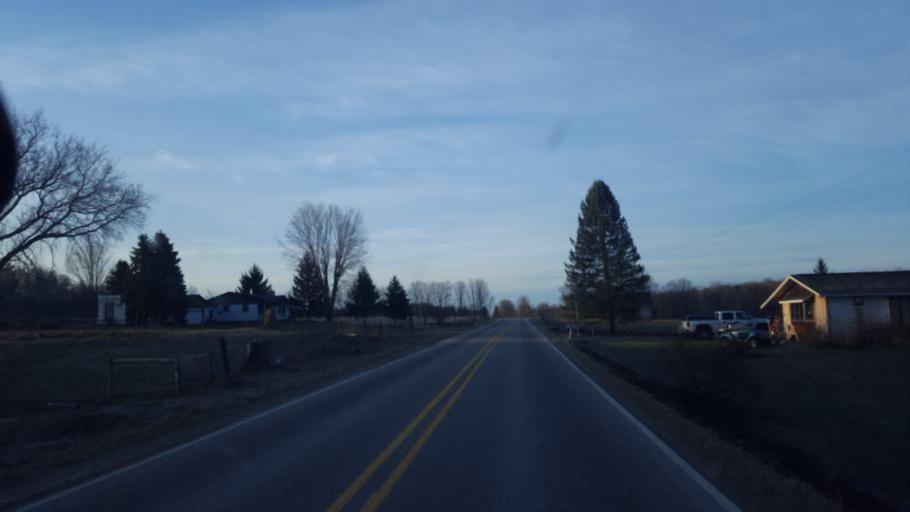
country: US
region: Michigan
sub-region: Isabella County
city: Lake Isabella
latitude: 43.5337
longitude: -85.0261
